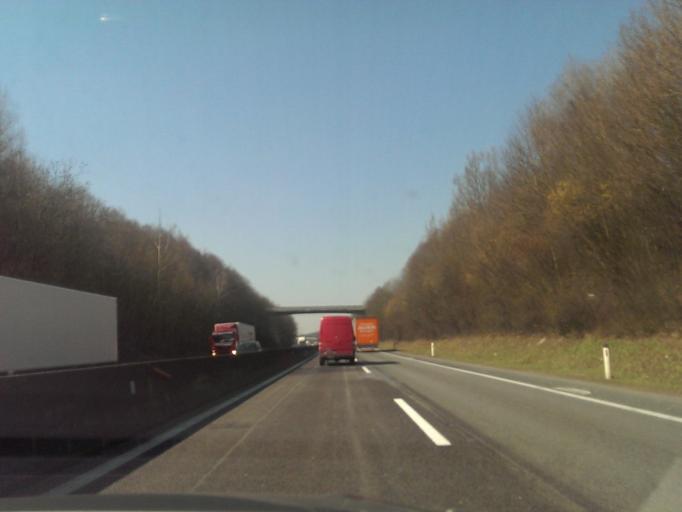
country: AT
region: Upper Austria
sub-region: Politischer Bezirk Ried im Innkreis
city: Ried im Innkreis
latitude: 48.2289
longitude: 13.5999
